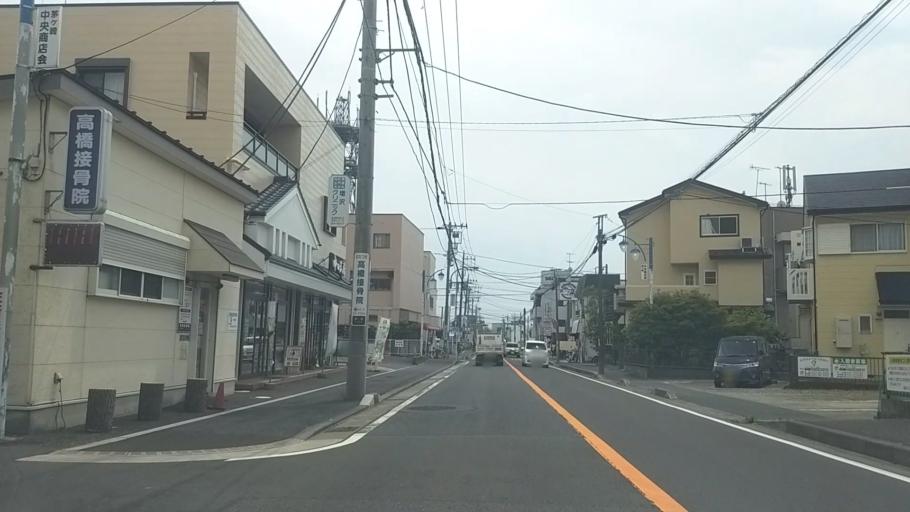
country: JP
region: Kanagawa
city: Chigasaki
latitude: 35.3483
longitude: 139.4139
